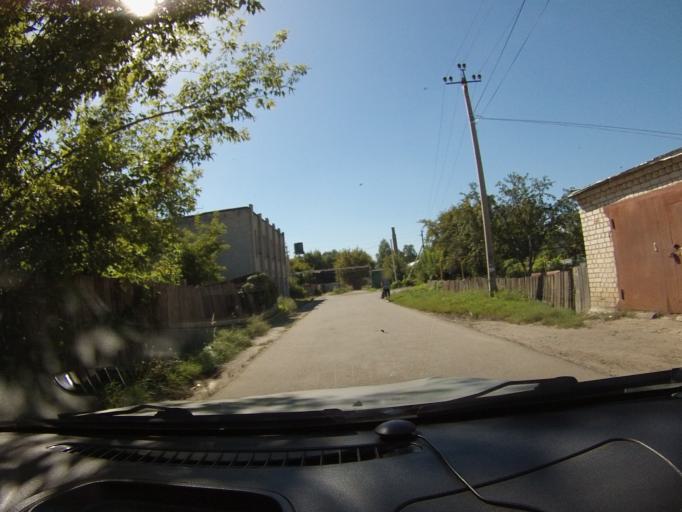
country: RU
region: Tambov
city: Donskoye
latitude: 52.7619
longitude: 41.4731
